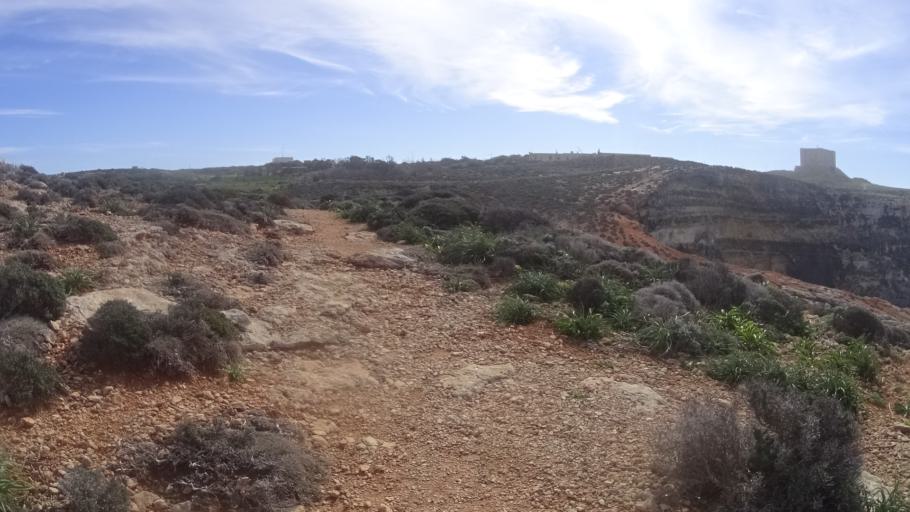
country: MT
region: Il-Qala
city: Qala
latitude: 36.0103
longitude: 14.3291
